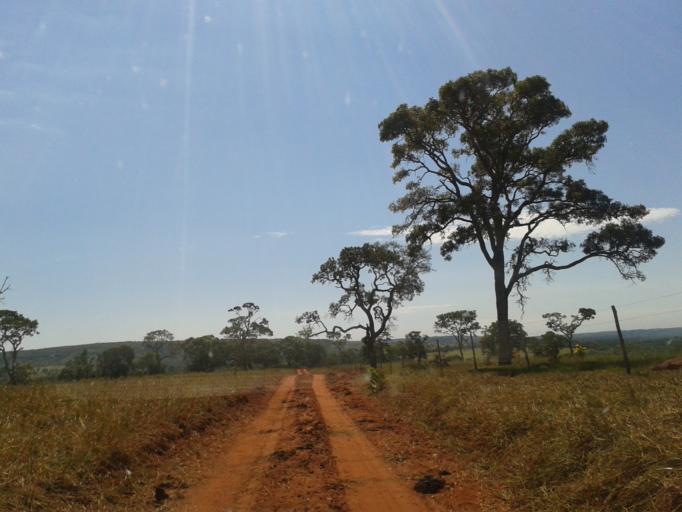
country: BR
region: Minas Gerais
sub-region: Campina Verde
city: Campina Verde
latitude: -19.4007
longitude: -49.7658
